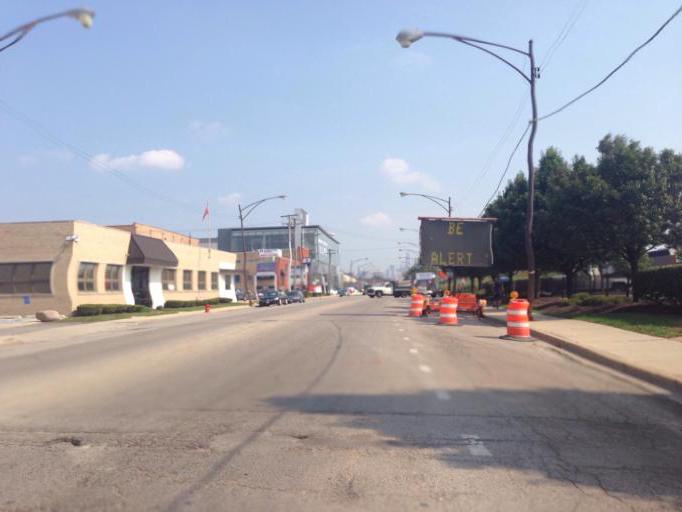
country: US
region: Illinois
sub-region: Cook County
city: Chicago
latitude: 41.9283
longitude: -87.6824
